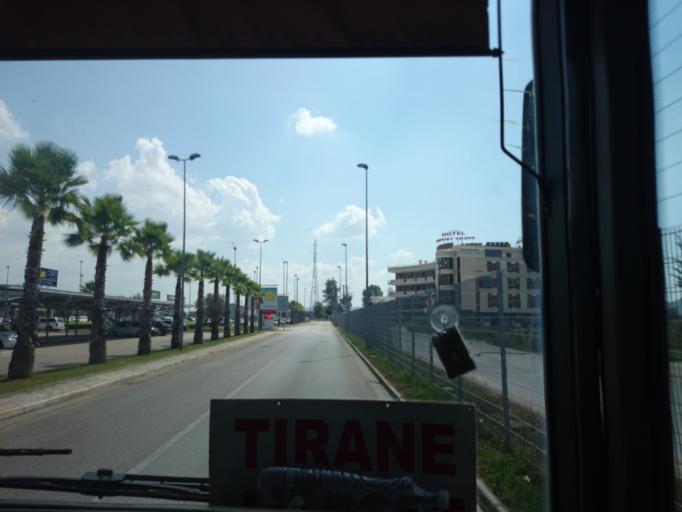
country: AL
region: Tirane
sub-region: Rrethi i Tiranes
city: Preze
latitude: 41.4178
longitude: 19.7125
